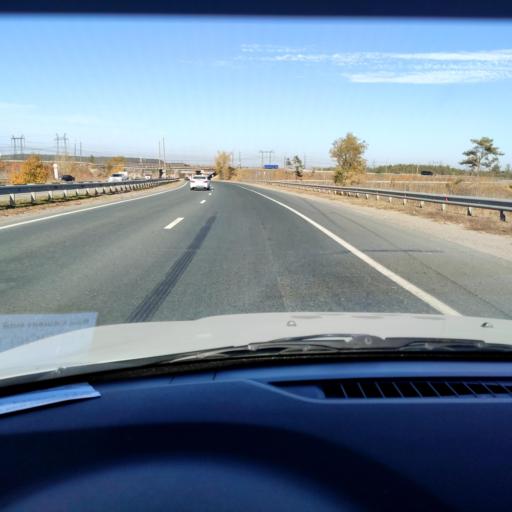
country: RU
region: Samara
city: Zhigulevsk
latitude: 53.5156
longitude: 49.5370
